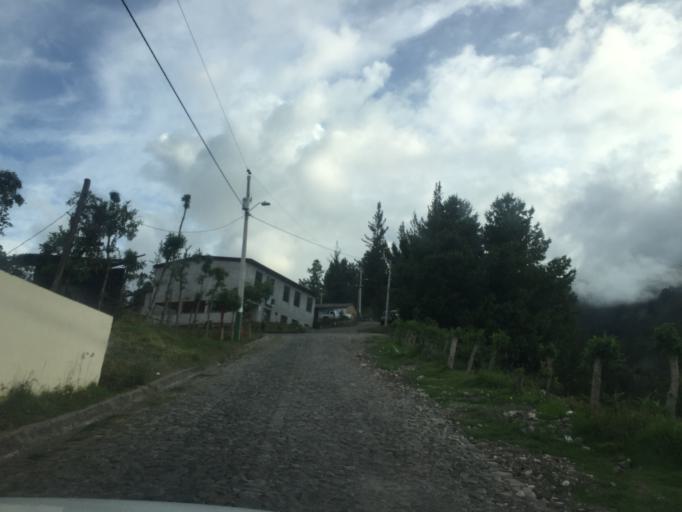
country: EC
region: Imbabura
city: Ibarra
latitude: 0.2851
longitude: -78.1385
